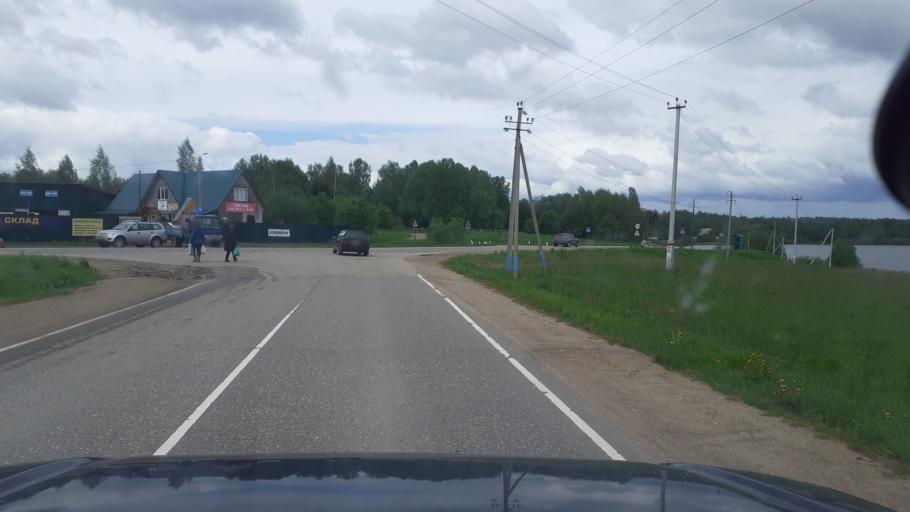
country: RU
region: Moskovskaya
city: Sychevo
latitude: 55.9686
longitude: 36.2230
